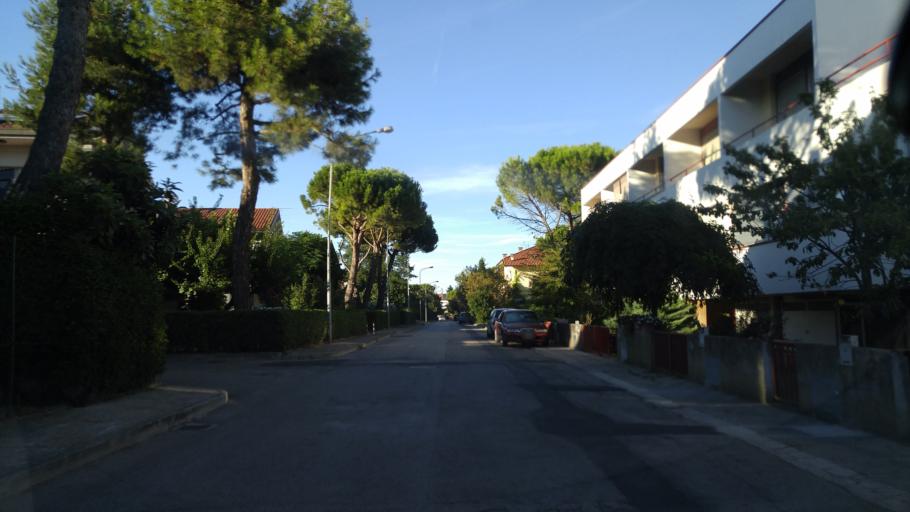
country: IT
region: The Marches
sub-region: Provincia di Pesaro e Urbino
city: Fano
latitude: 43.8308
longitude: 13.0201
